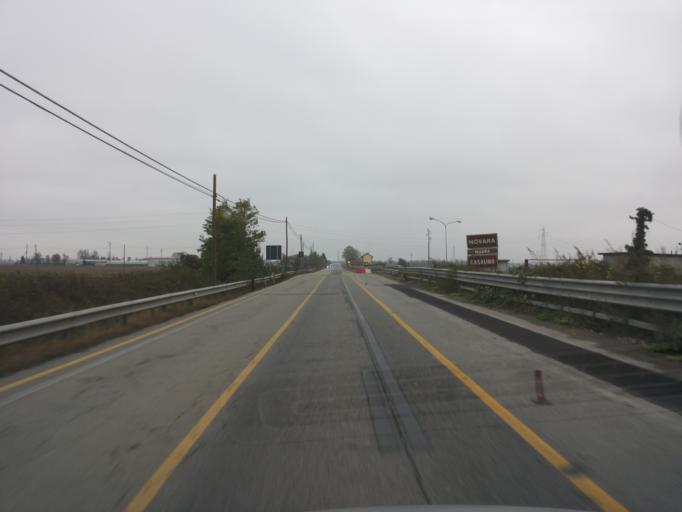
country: IT
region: Piedmont
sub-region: Provincia di Novara
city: Lumellogno
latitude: 45.4113
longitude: 8.5608
